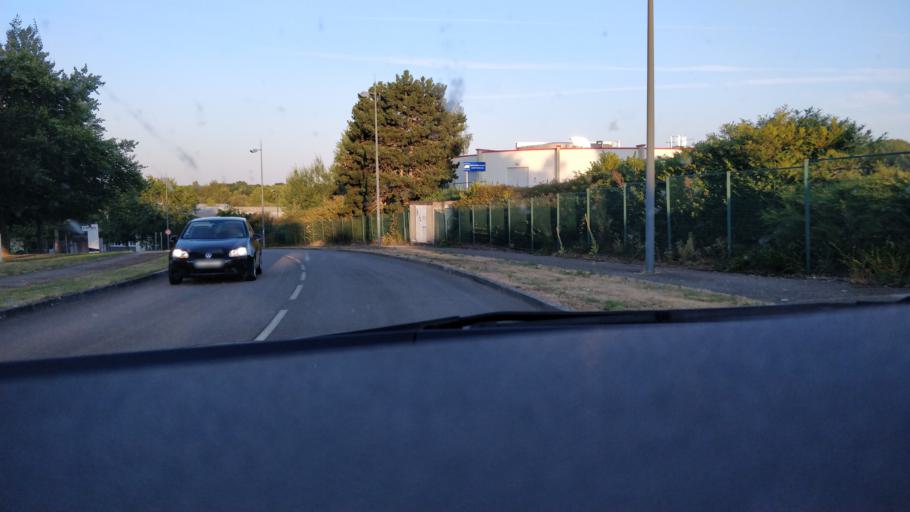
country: FR
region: Limousin
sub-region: Departement de la Haute-Vienne
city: Le Palais-sur-Vienne
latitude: 45.8647
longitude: 1.2946
